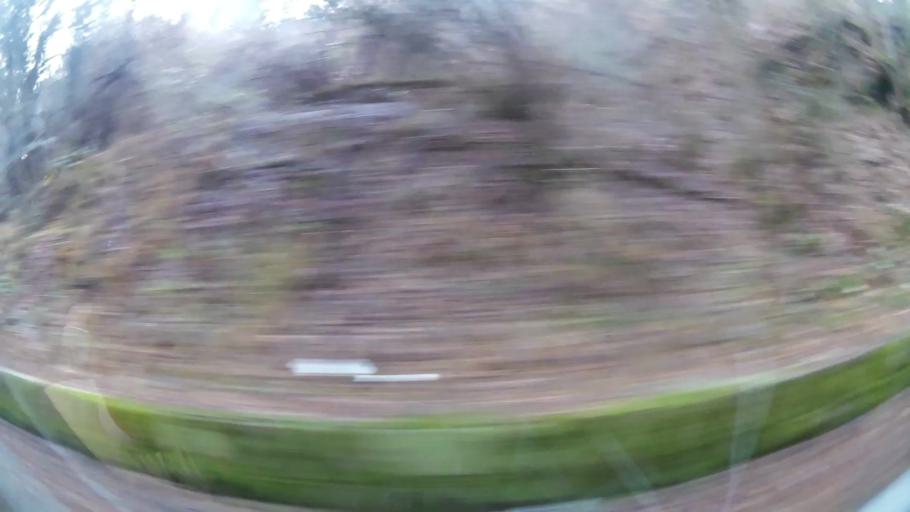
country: BG
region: Sofia-Capital
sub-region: Stolichna Obshtina
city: Sofia
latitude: 42.5878
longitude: 23.4262
